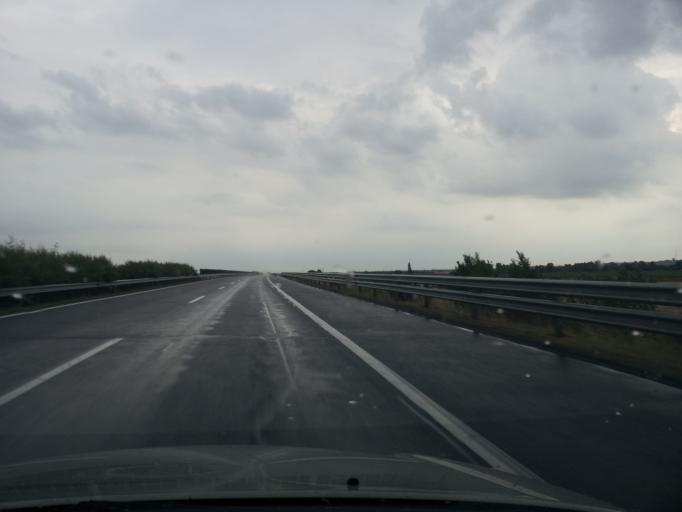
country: HU
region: Borsod-Abauj-Zemplen
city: Onod
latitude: 47.9542
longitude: 20.8869
